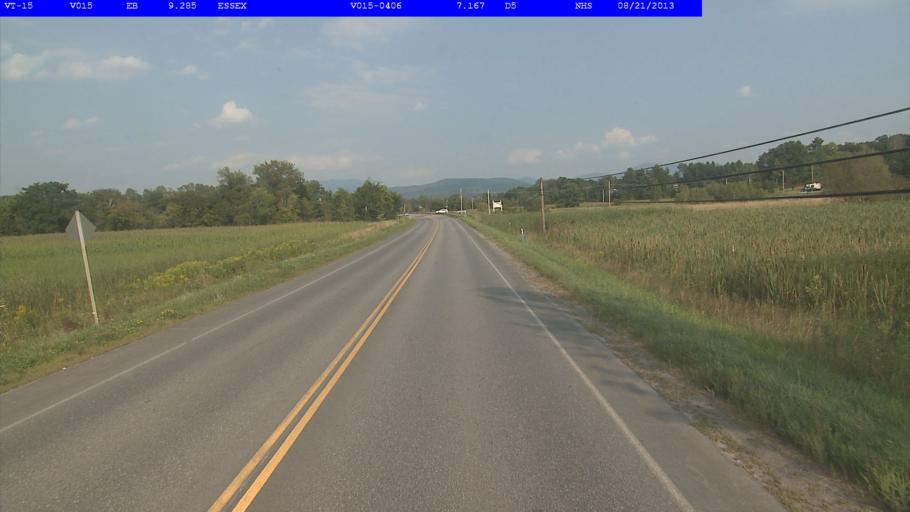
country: US
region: Vermont
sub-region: Chittenden County
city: Jericho
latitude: 44.5017
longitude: -73.0263
